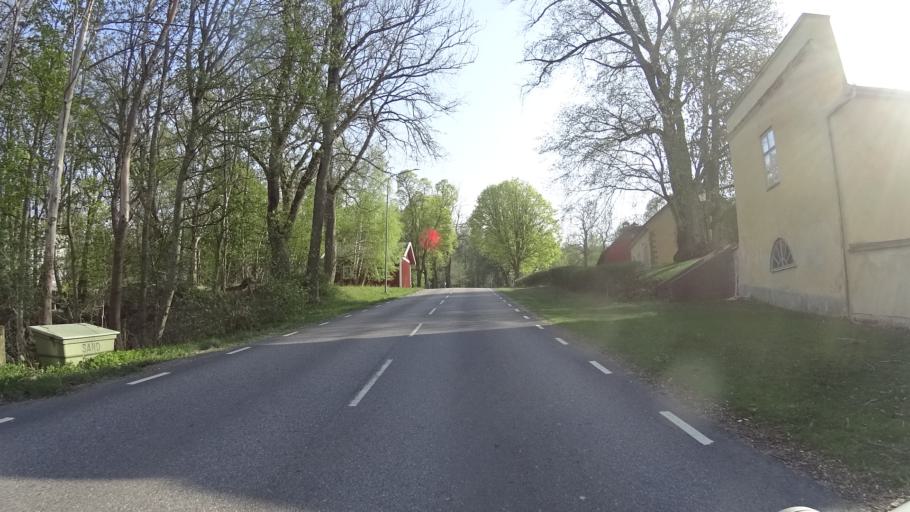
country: SE
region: Vaestra Goetaland
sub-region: Gotene Kommun
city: Goetene
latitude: 58.6255
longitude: 13.4270
